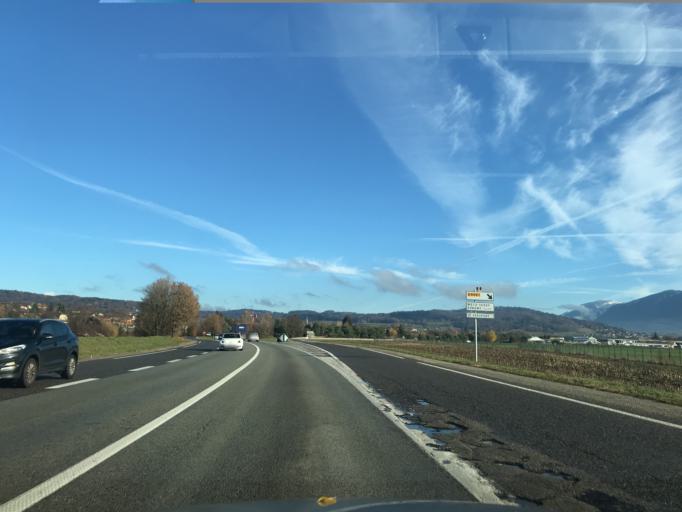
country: FR
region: Rhone-Alpes
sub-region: Departement de la Haute-Savoie
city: Metz-Tessy
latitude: 45.9335
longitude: 6.0998
